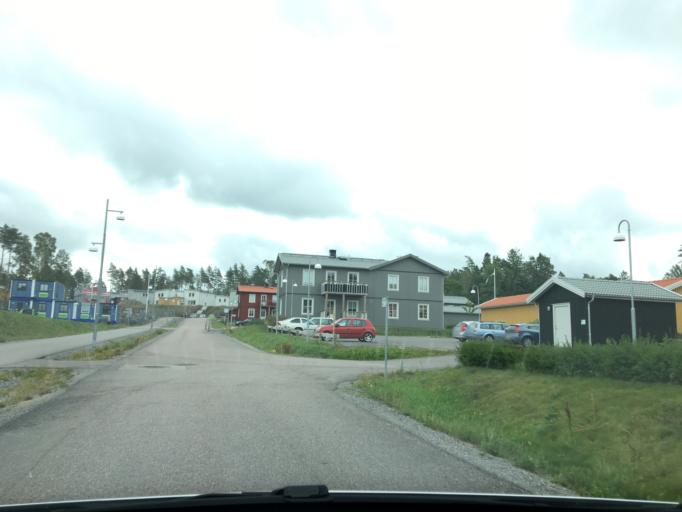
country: SE
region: Vaestra Goetaland
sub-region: Ale Kommun
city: Alvangen
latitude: 57.9482
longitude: 12.1183
